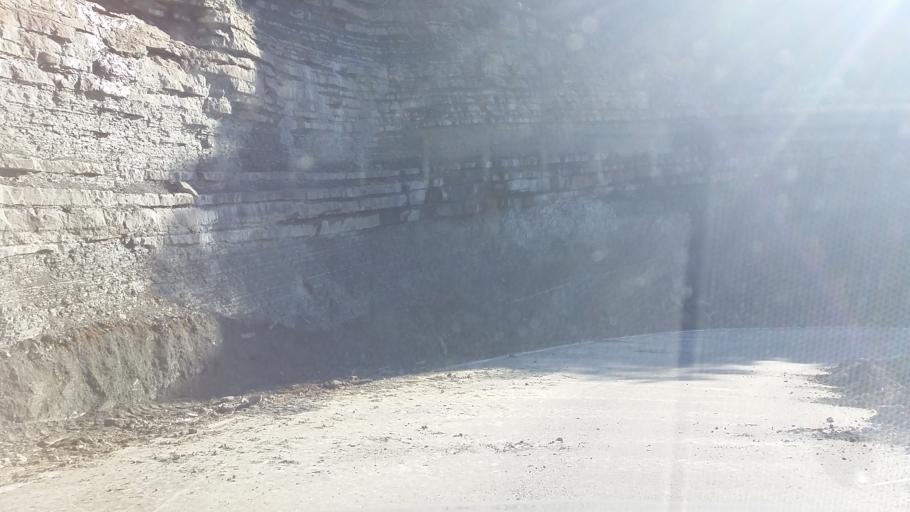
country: GR
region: West Greece
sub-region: Nomos Aitolias kai Akarnanias
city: Krikellos
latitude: 38.9731
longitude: 21.2764
